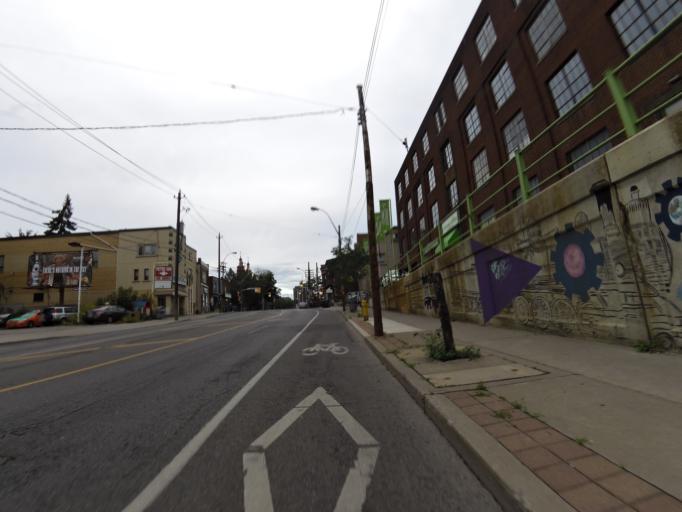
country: CA
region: Ontario
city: Toronto
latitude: 43.6645
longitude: -79.4565
